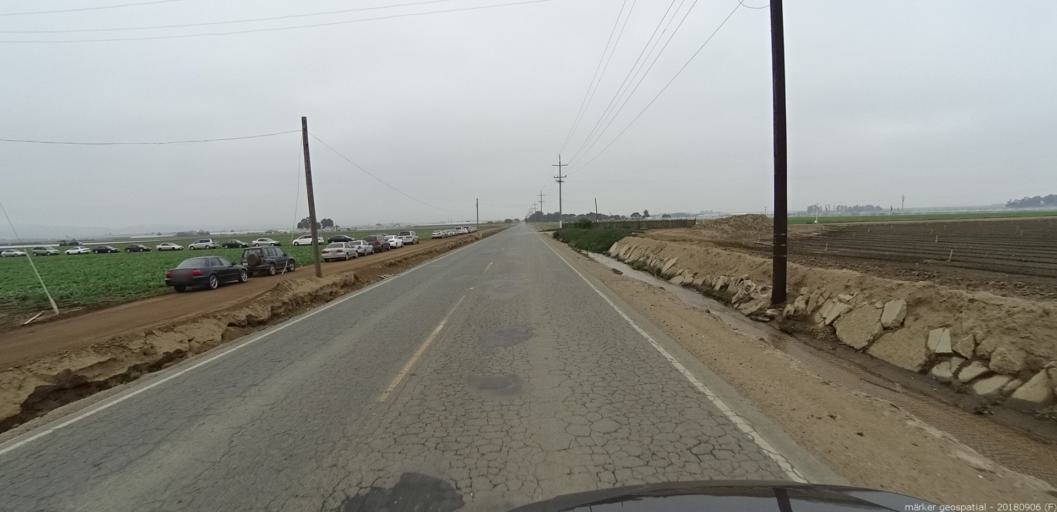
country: US
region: California
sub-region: Monterey County
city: Chualar
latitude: 36.6345
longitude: -121.5533
